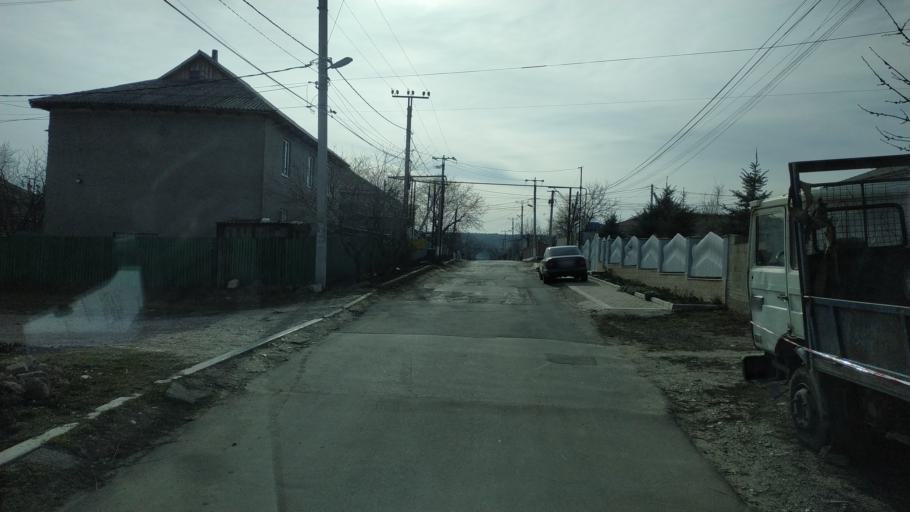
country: MD
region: Chisinau
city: Vatra
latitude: 47.0789
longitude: 28.6864
